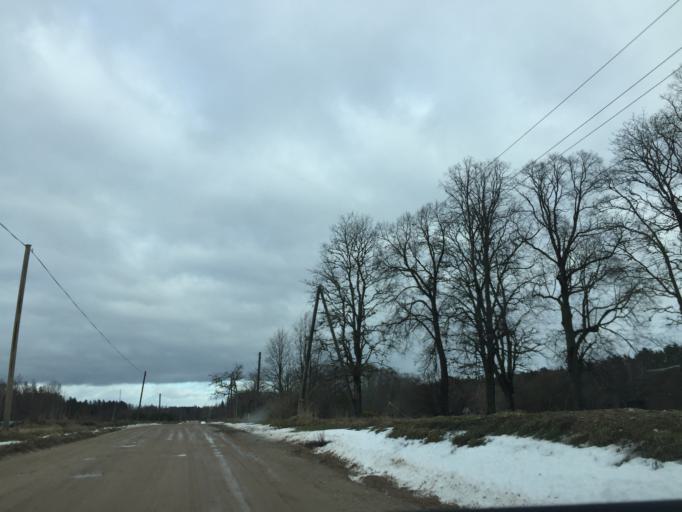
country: LV
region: Salacgrivas
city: Ainazi
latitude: 57.8516
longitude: 24.4888
